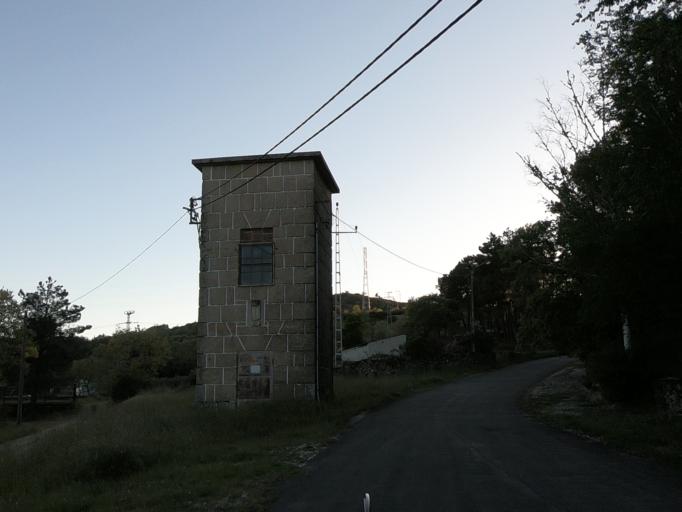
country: PT
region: Vila Real
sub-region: Sabrosa
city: Sabrosa
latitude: 41.3466
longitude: -7.6226
